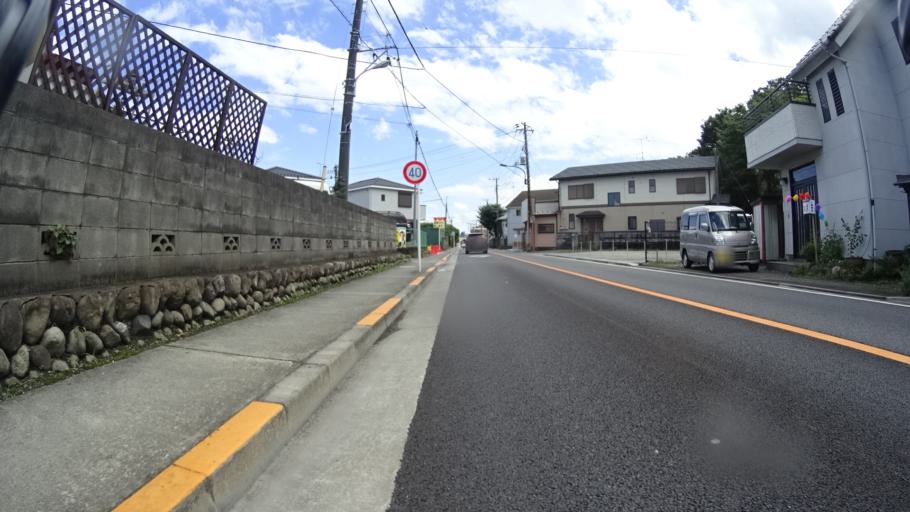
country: JP
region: Tokyo
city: Fussa
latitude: 35.7401
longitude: 139.3229
